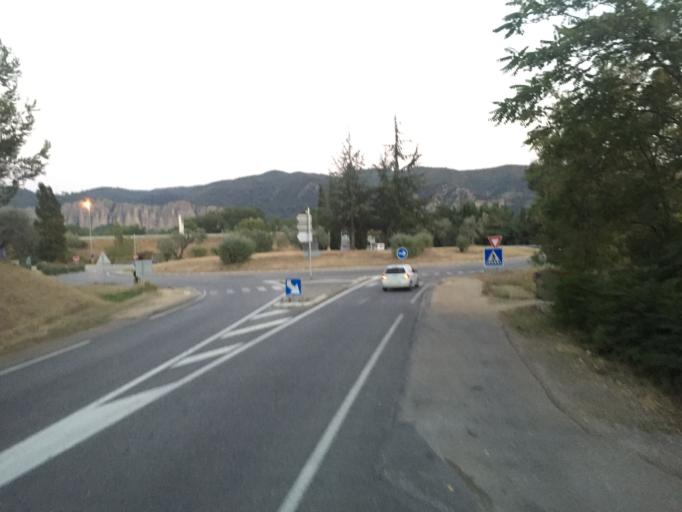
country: FR
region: Provence-Alpes-Cote d'Azur
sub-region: Departement des Alpes-de-Haute-Provence
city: Les Mees
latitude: 44.0384
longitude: 5.9610
